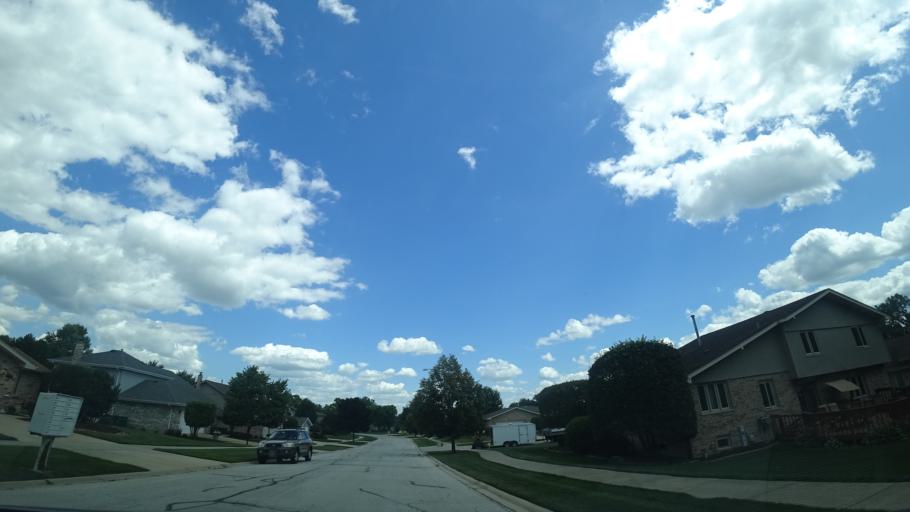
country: US
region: Illinois
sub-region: Will County
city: Homer Glen
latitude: 41.5756
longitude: -87.9030
